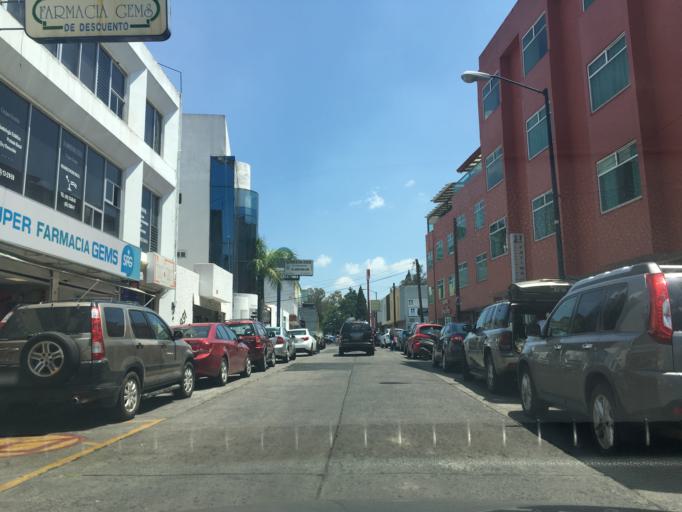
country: MX
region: Michoacan
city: Morelia
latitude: 19.6965
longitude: -101.1835
